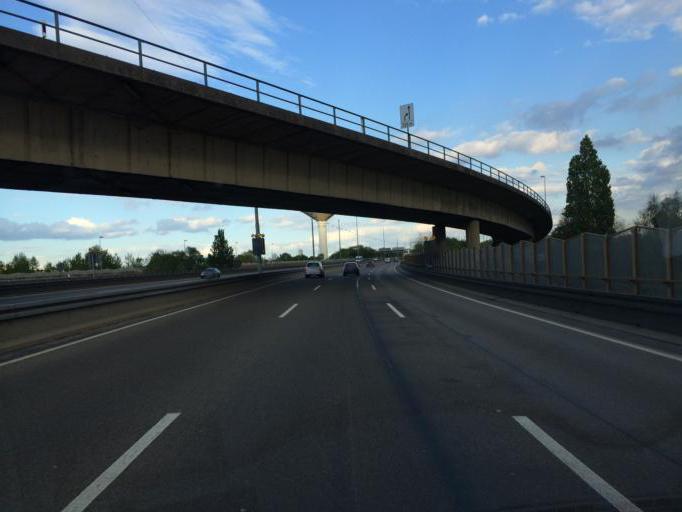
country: DE
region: North Rhine-Westphalia
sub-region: Regierungsbezirk Koln
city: Leverkusen
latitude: 51.0387
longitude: 6.9746
